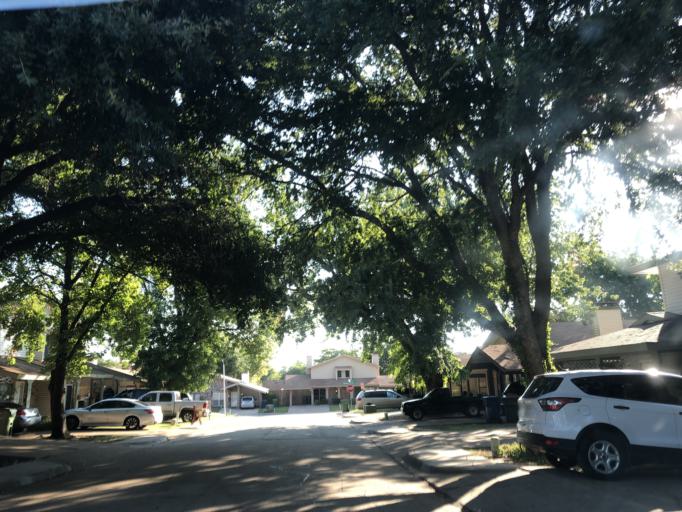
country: US
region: Texas
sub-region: Dallas County
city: Garland
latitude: 32.8608
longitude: -96.6389
